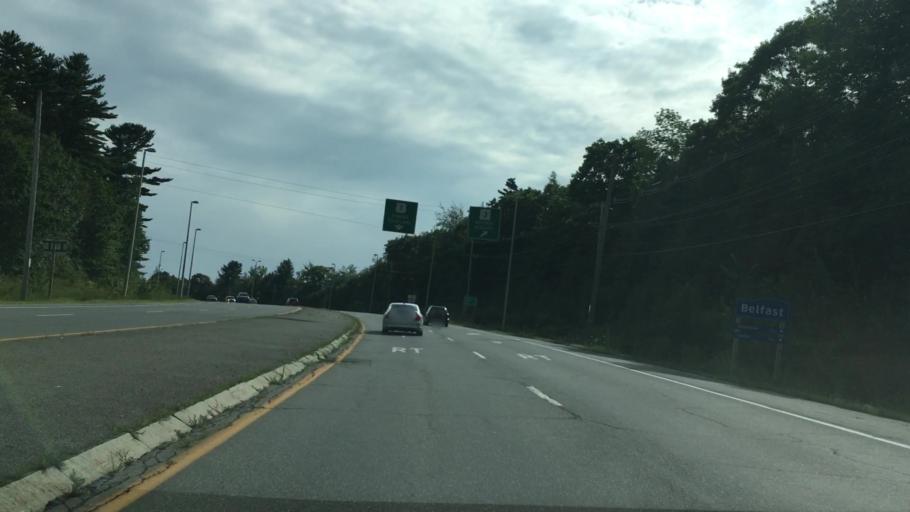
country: US
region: Maine
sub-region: Waldo County
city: Belfast
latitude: 44.4294
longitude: -69.0206
